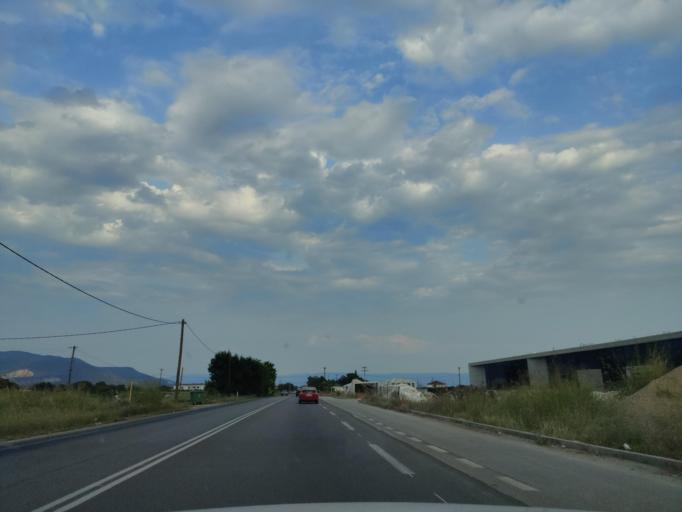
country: GR
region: East Macedonia and Thrace
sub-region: Nomos Dramas
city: Xiropotamos
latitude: 41.1583
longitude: 24.0961
